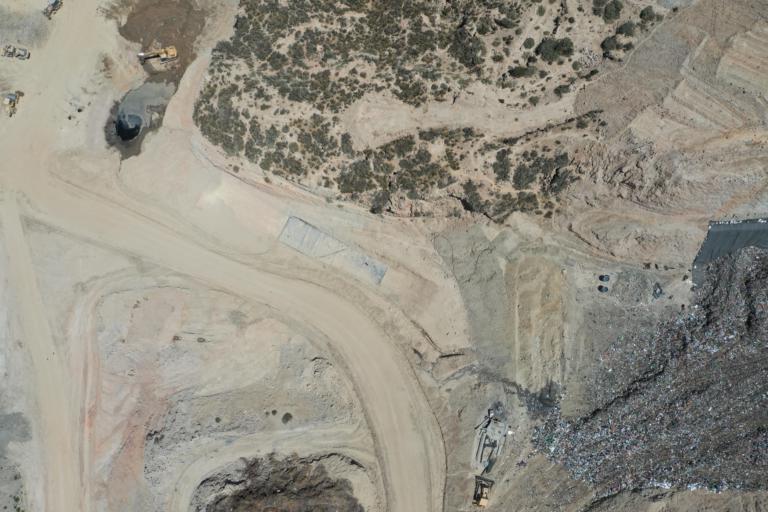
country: BO
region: La Paz
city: La Paz
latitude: -16.5563
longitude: -68.1290
